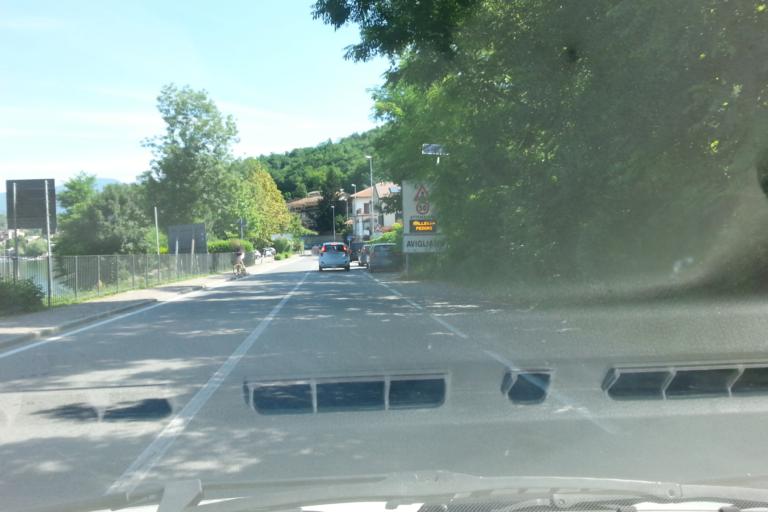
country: IT
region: Piedmont
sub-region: Provincia di Torino
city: Avigliana
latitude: 45.0627
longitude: 7.3926
